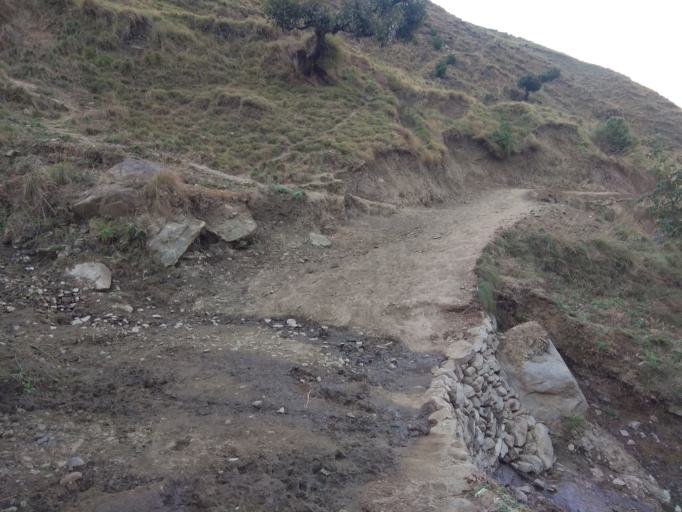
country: NP
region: Mid Western
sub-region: Karnali Zone
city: Jumla
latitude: 29.3196
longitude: 81.7236
